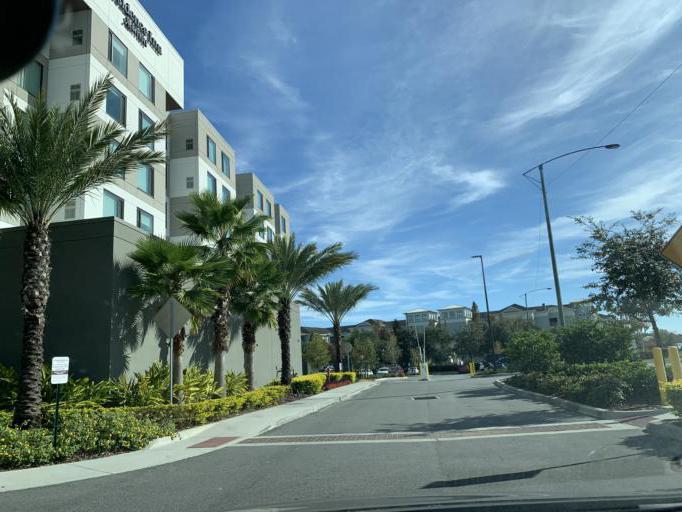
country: US
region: Florida
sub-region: Orange County
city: Oak Ridge
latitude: 28.4843
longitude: -81.4351
